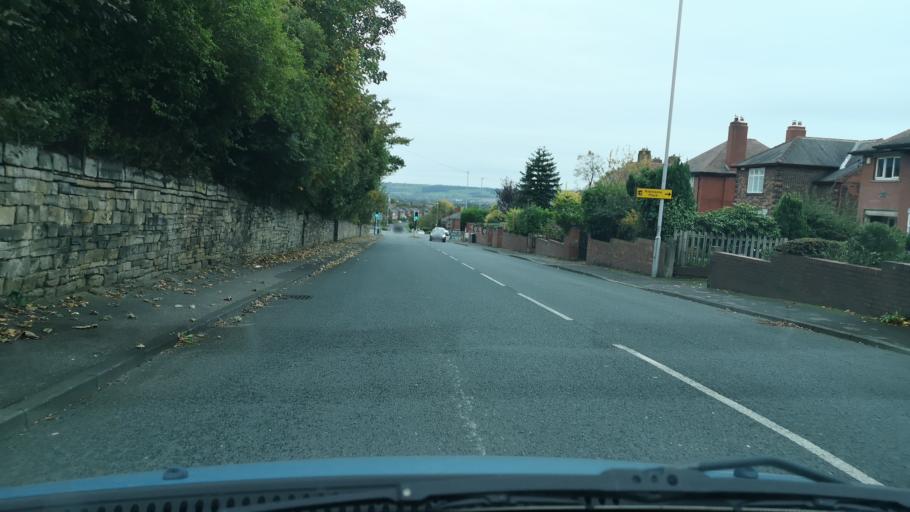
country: GB
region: England
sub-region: Kirklees
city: Heckmondwike
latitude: 53.7169
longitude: -1.6801
